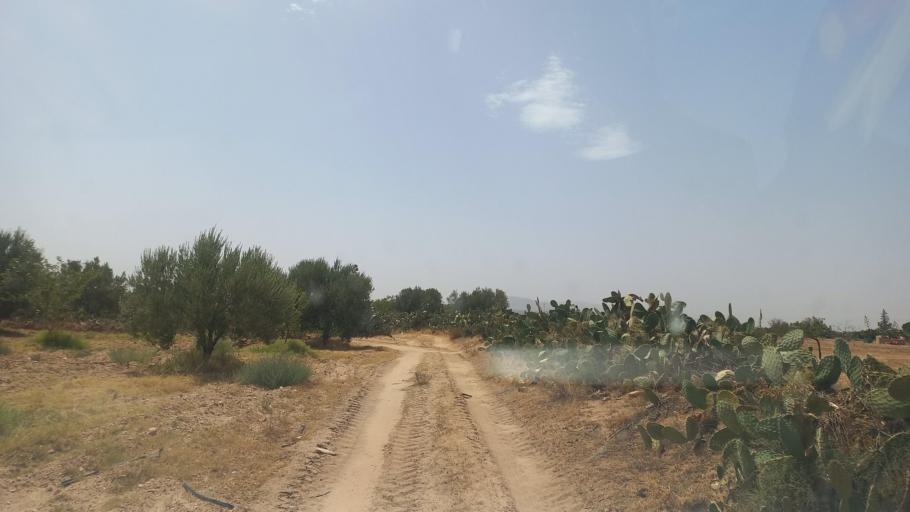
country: TN
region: Al Qasrayn
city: Kasserine
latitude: 35.2602
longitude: 9.0053
